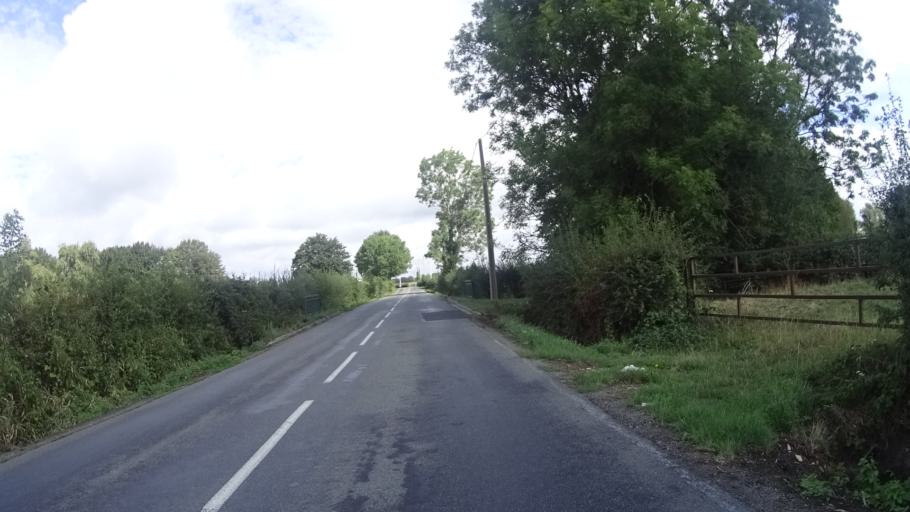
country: FR
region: Nord-Pas-de-Calais
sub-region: Departement du Nord
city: Landrecies
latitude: 50.0784
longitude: 3.6497
